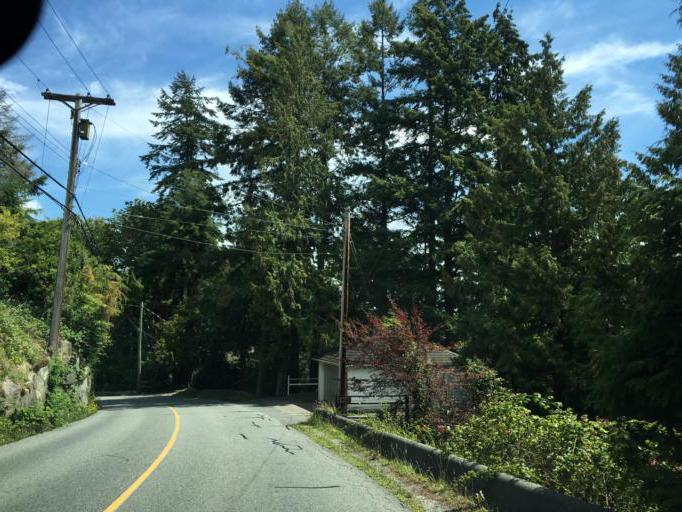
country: CA
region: British Columbia
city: West Vancouver
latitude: 49.3410
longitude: -123.2466
